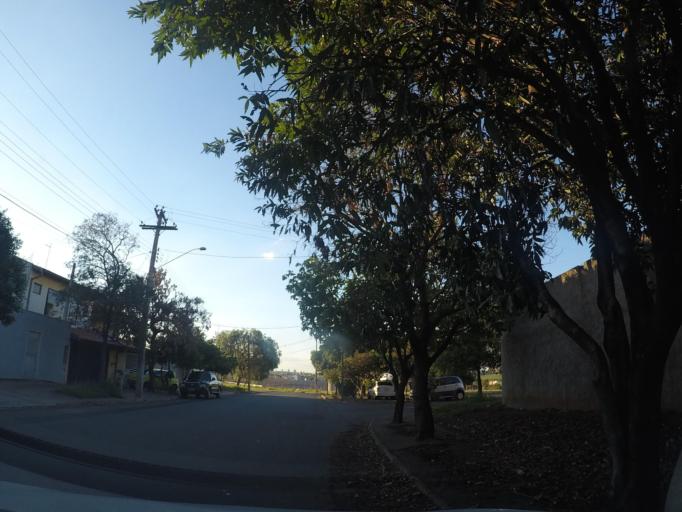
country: BR
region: Sao Paulo
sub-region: Sumare
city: Sumare
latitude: -22.8207
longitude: -47.2511
